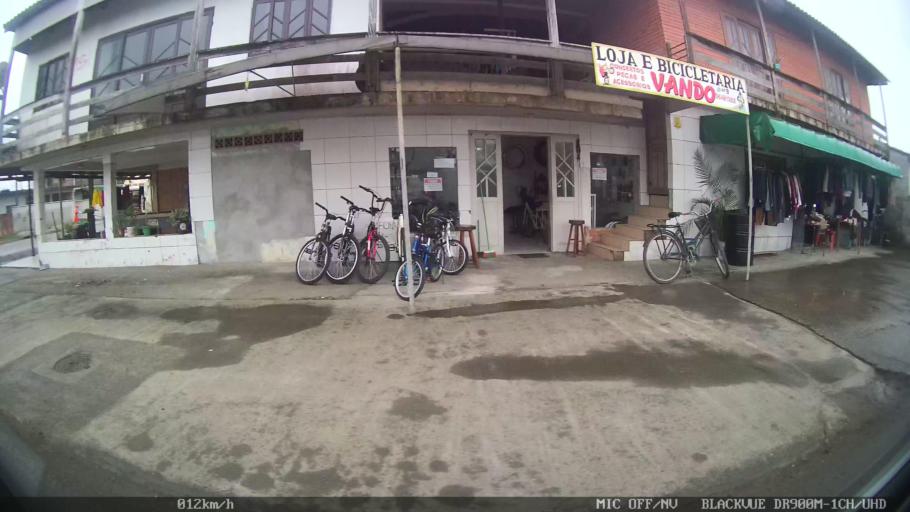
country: BR
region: Santa Catarina
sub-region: Joinville
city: Joinville
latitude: -26.2091
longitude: -48.8326
